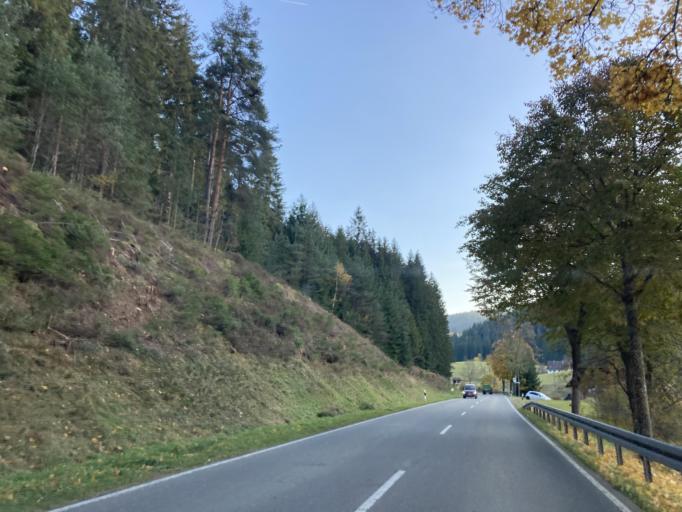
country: DE
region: Baden-Wuerttemberg
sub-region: Freiburg Region
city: Vohrenbach
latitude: 48.0000
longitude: 8.3039
